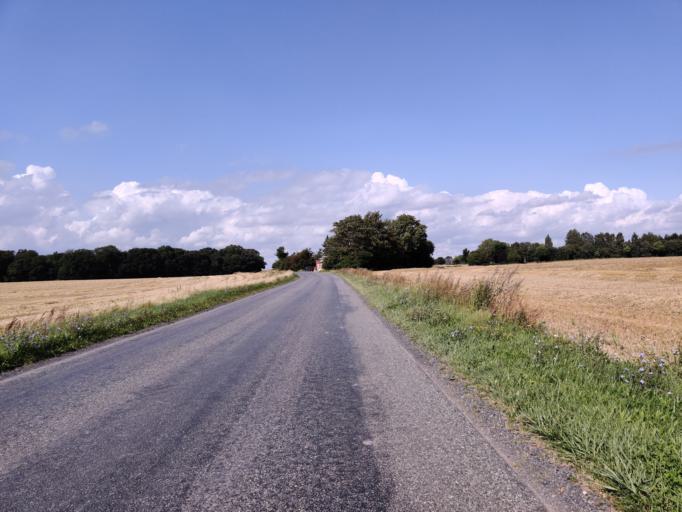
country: DK
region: Zealand
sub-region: Guldborgsund Kommune
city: Nykobing Falster
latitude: 54.6399
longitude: 11.8970
